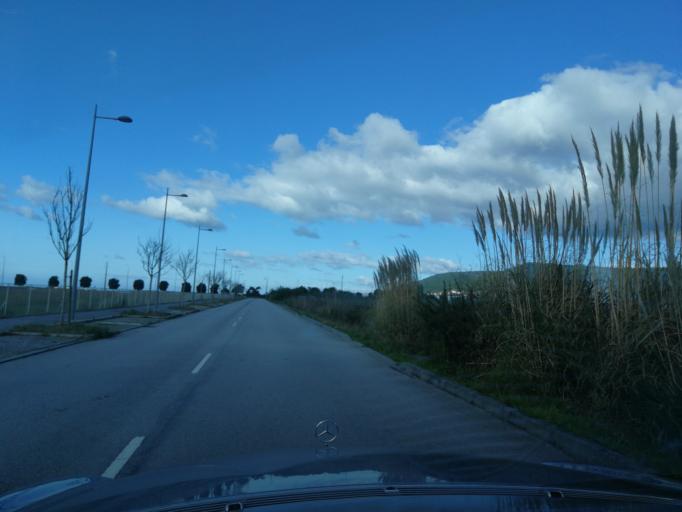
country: PT
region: Viana do Castelo
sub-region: Viana do Castelo
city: Viana do Castelo
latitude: 41.6974
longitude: -8.8474
